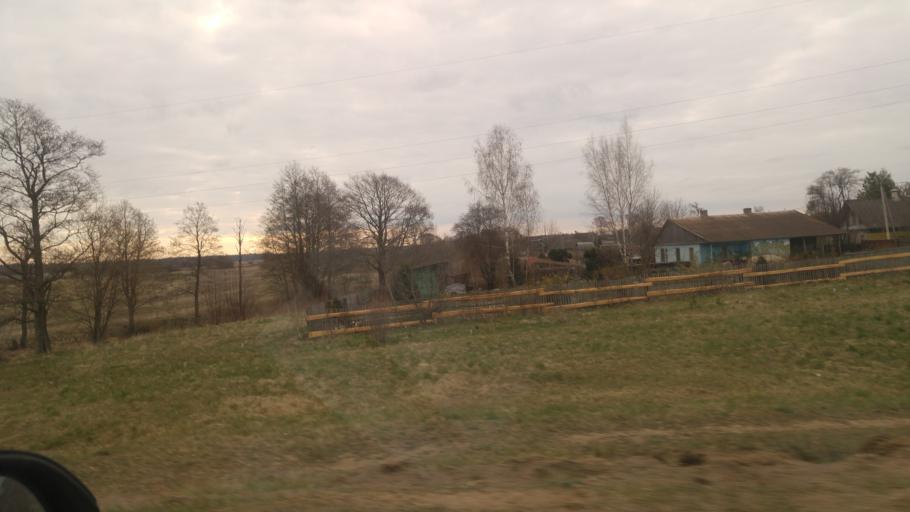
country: BY
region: Minsk
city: Pukhavichy
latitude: 53.7025
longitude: 28.2313
